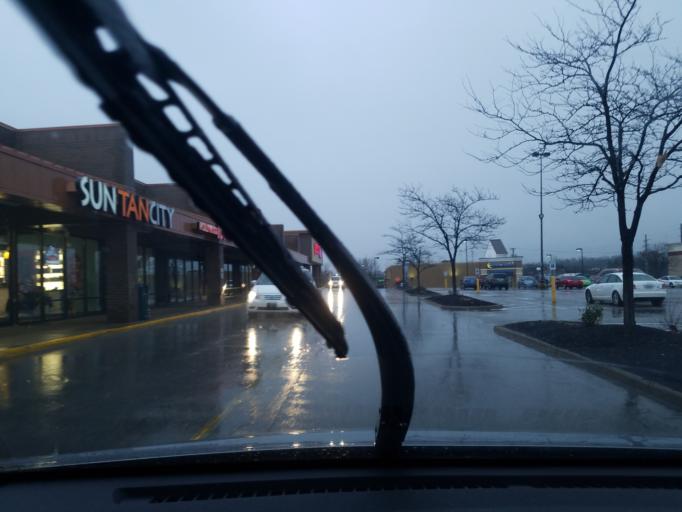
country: US
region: Kentucky
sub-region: Jefferson County
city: Middletown
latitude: 38.2450
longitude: -85.5199
